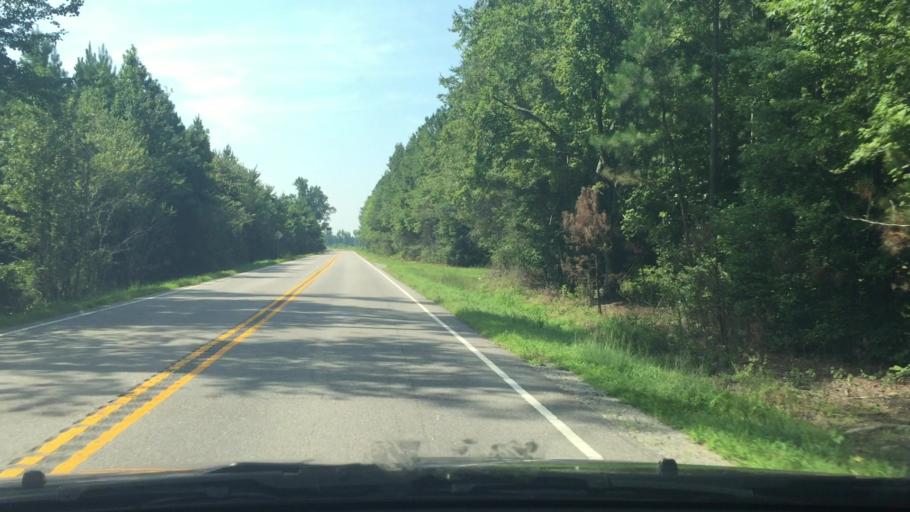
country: US
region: Virginia
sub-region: Southampton County
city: Courtland
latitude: 36.8081
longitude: -77.1278
